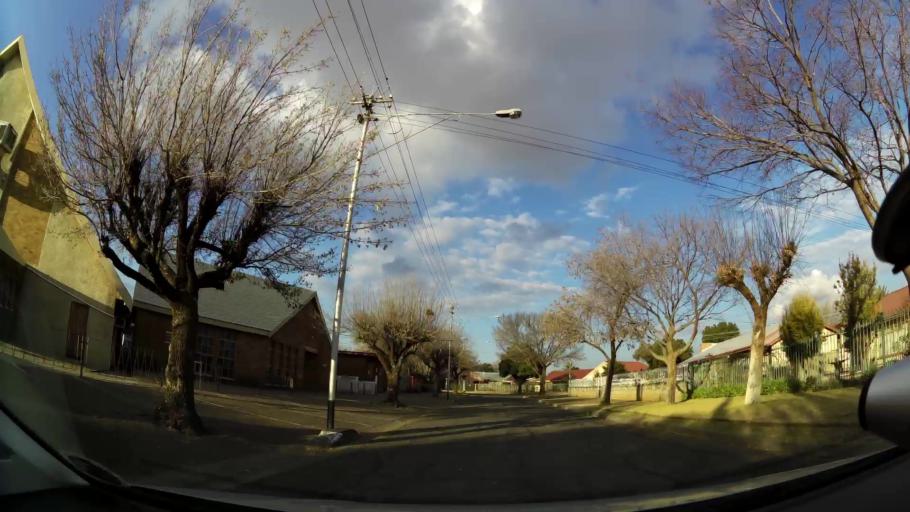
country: ZA
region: Orange Free State
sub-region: Mangaung Metropolitan Municipality
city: Bloemfontein
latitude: -29.1421
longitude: 26.1945
